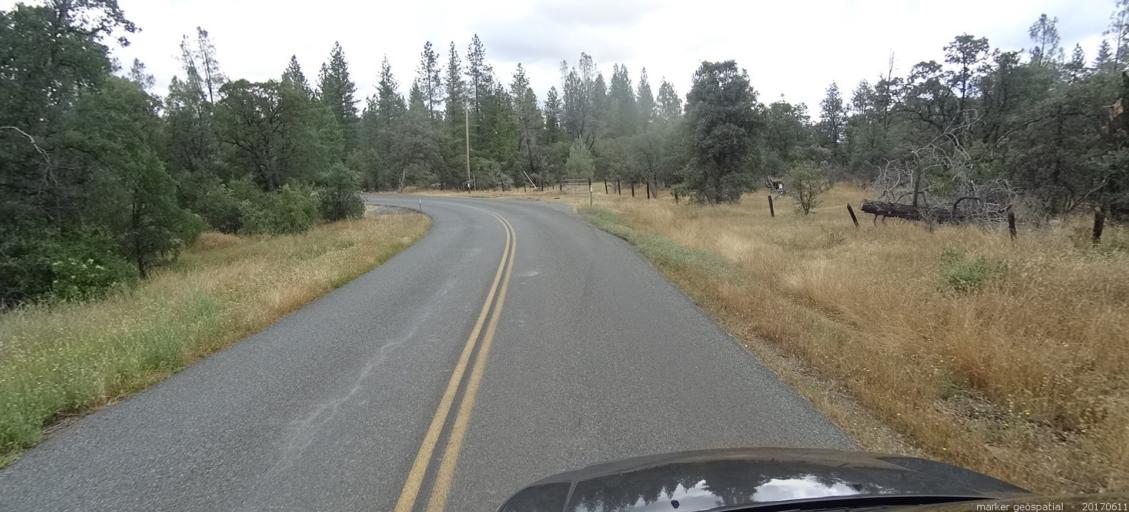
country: US
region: California
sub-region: Butte County
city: Berry Creek
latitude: 39.6457
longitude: -121.5316
